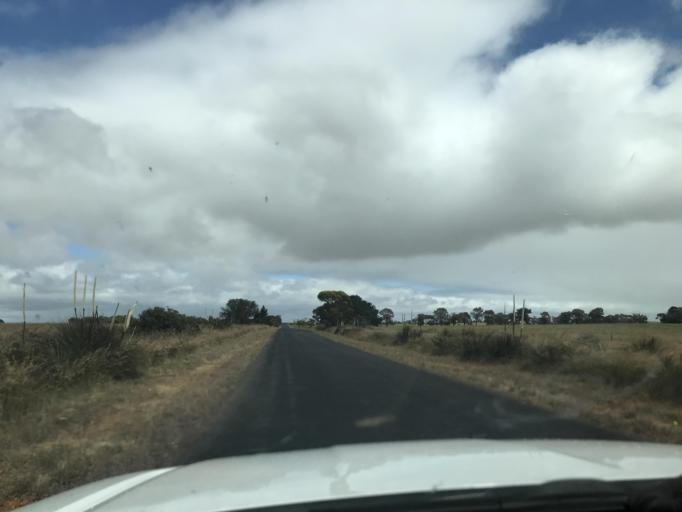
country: AU
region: South Australia
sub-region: Tatiara
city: Bordertown
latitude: -36.1361
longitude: 141.1905
